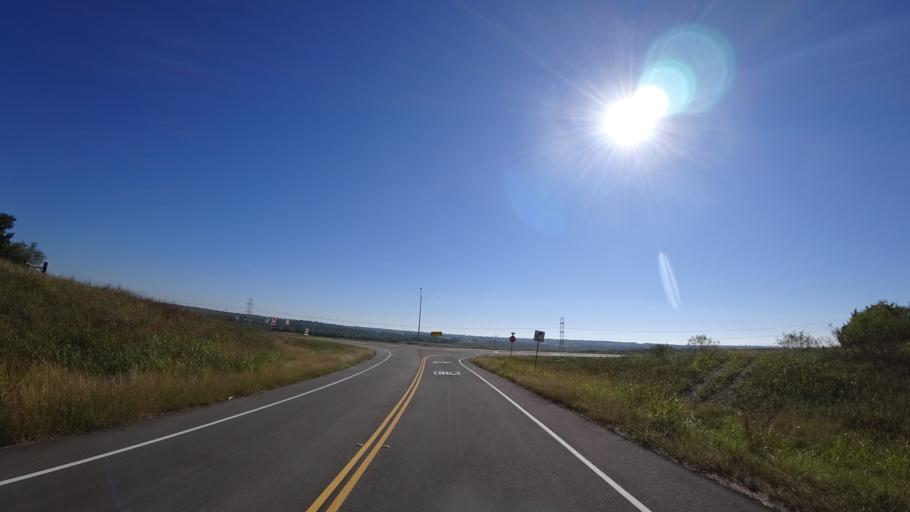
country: US
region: Texas
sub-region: Travis County
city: Manor
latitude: 30.2993
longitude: -97.5712
